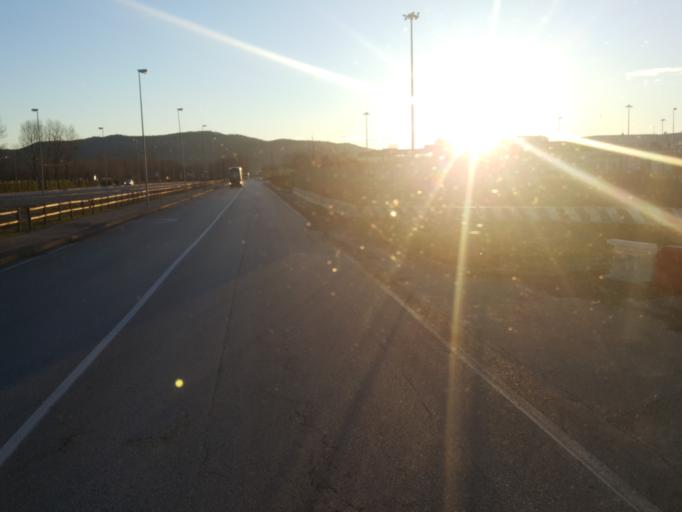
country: IT
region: Friuli Venezia Giulia
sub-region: Provincia di Gorizia
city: Monfalcone
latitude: 45.7928
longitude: 13.5584
